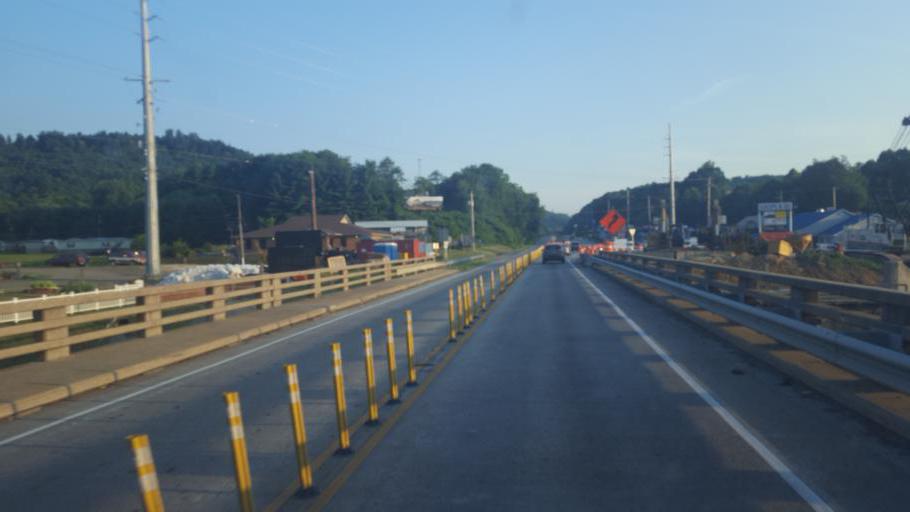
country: US
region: Virginia
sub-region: Scott County
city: Weber City
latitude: 36.6086
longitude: -82.5687
